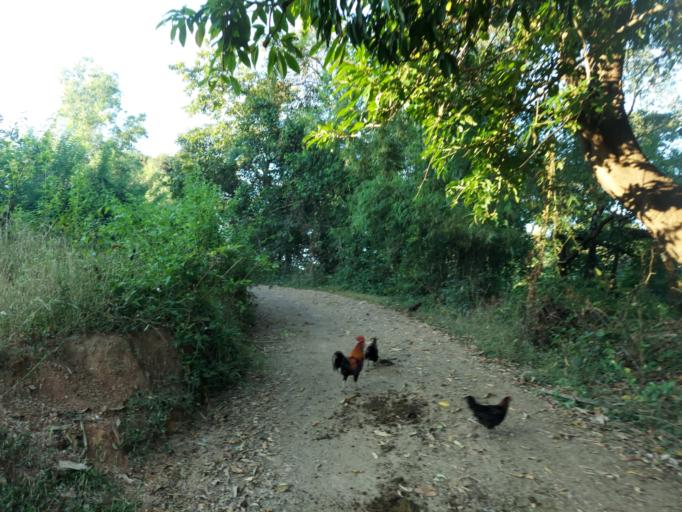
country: IN
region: Maharashtra
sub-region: Sindhudurg
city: Kudal
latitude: 16.0385
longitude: 73.6790
